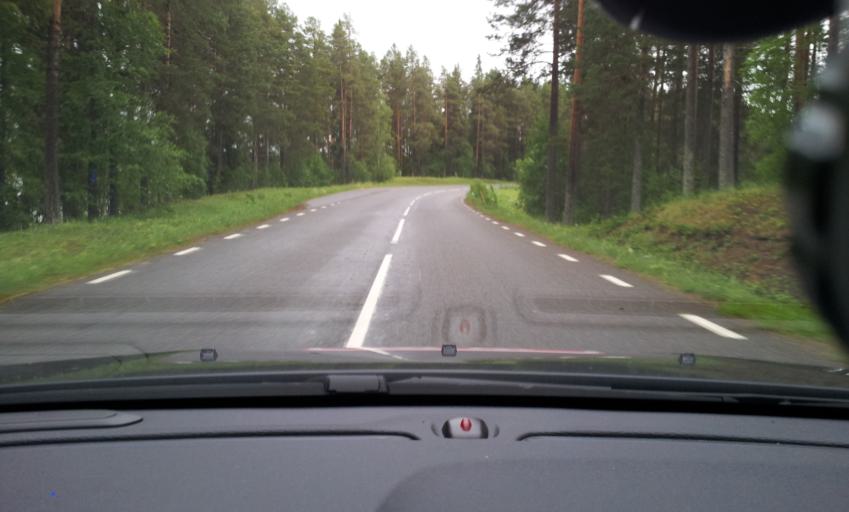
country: SE
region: Jaemtland
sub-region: Stroemsunds Kommun
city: Stroemsund
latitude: 63.5083
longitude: 15.4603
